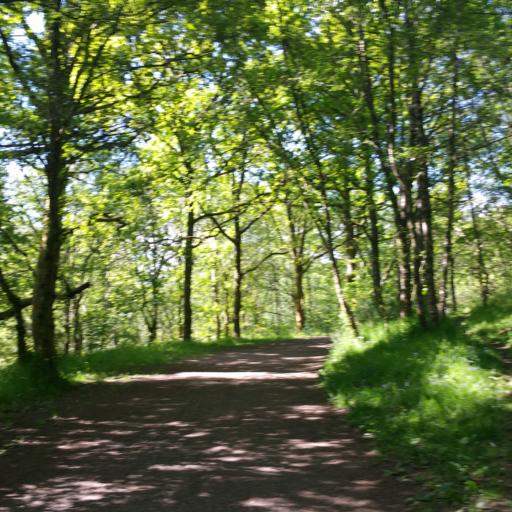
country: GB
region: Scotland
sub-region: East Dunbartonshire
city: Milngavie
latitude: 55.9576
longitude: -4.3315
